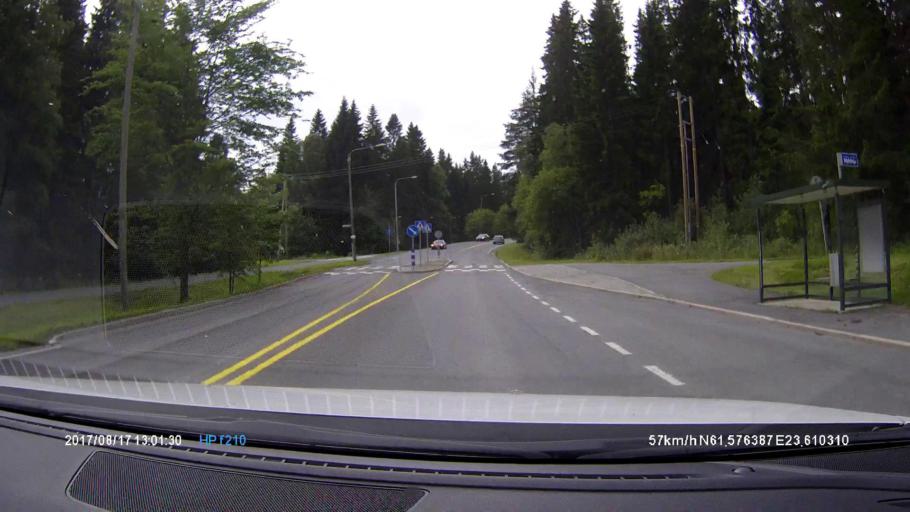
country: FI
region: Pirkanmaa
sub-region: Tampere
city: Yloejaervi
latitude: 61.5760
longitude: 23.6101
